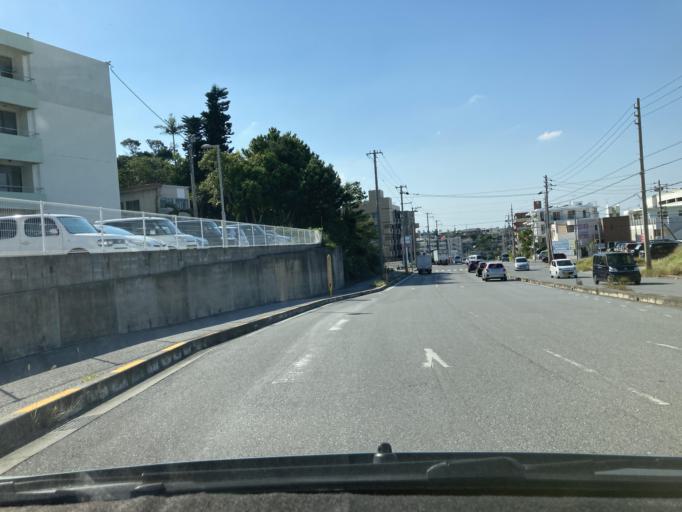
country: JP
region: Okinawa
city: Ginowan
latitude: 26.2360
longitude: 127.7246
